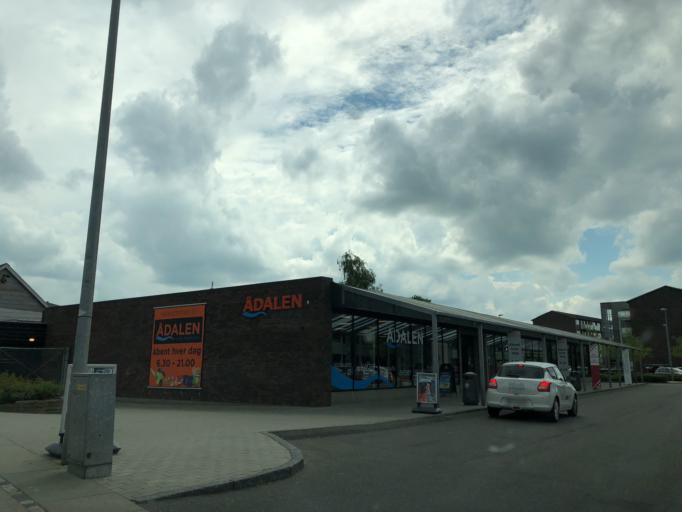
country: DK
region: Central Jutland
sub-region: Struer Kommune
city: Struer
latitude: 56.4870
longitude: 8.5911
